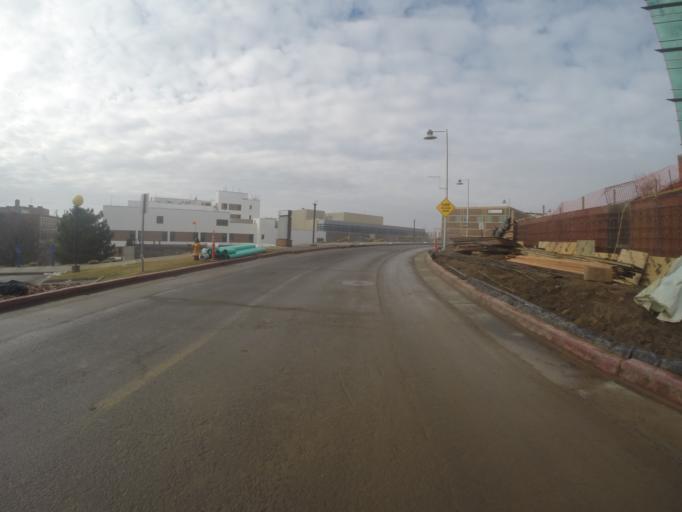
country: US
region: Utah
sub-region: Salt Lake County
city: Salt Lake City
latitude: 40.7719
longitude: -111.8348
